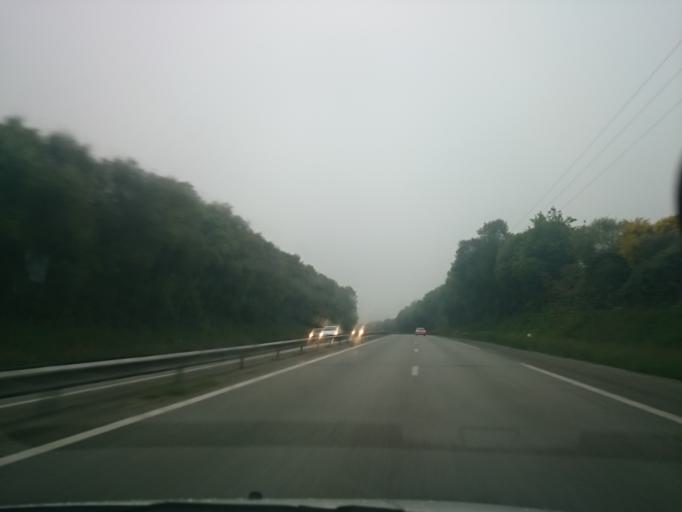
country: FR
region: Brittany
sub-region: Departement du Finistere
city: Briec
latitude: 48.1265
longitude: -4.0226
